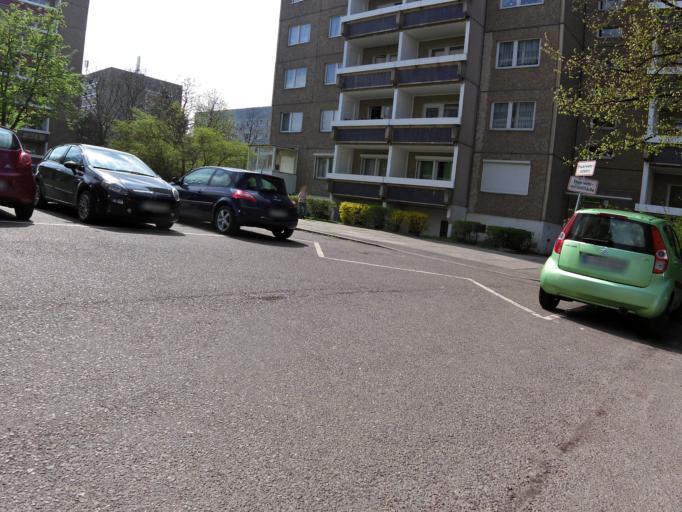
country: DE
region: Saxony
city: Markranstadt
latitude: 51.3204
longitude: 12.2749
